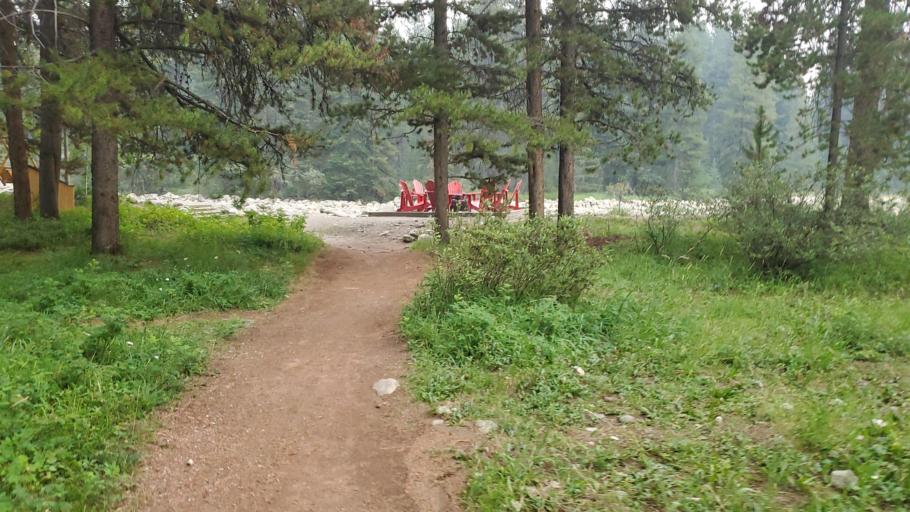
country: CA
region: Alberta
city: Lake Louise
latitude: 51.3486
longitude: -116.0685
